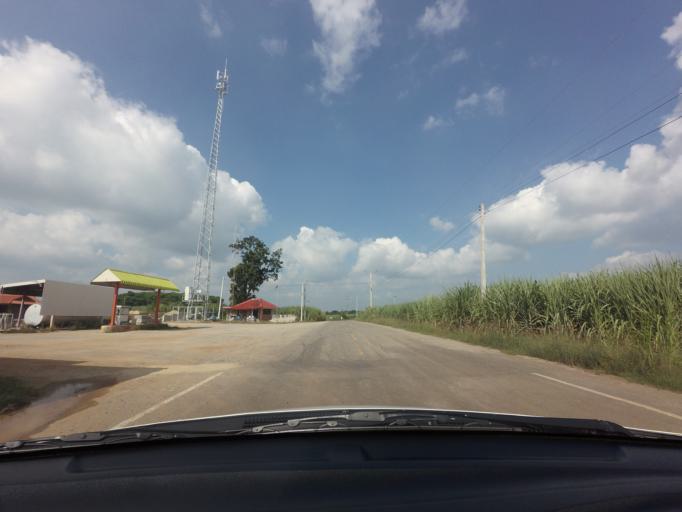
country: TH
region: Nakhon Ratchasima
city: Wang Nam Khiao
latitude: 14.5360
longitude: 101.6340
